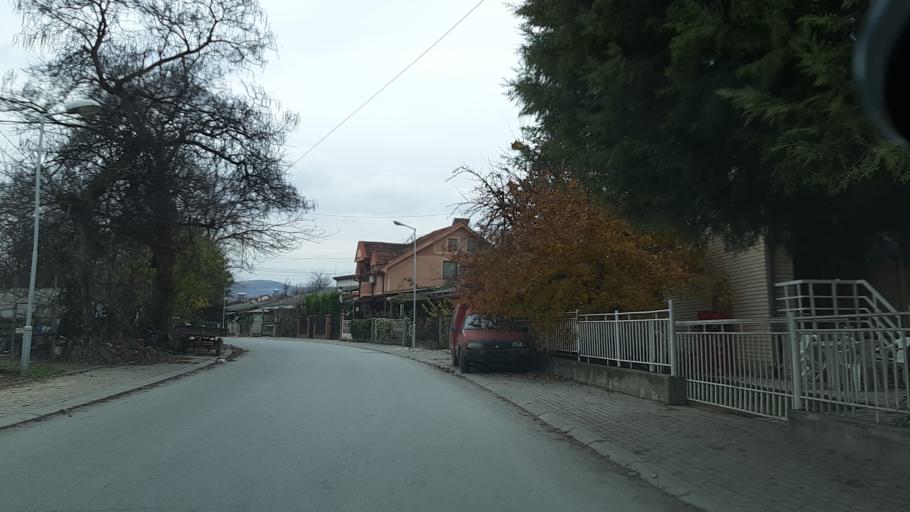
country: MK
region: Kisela Voda
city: Usje
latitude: 41.9740
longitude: 21.4782
